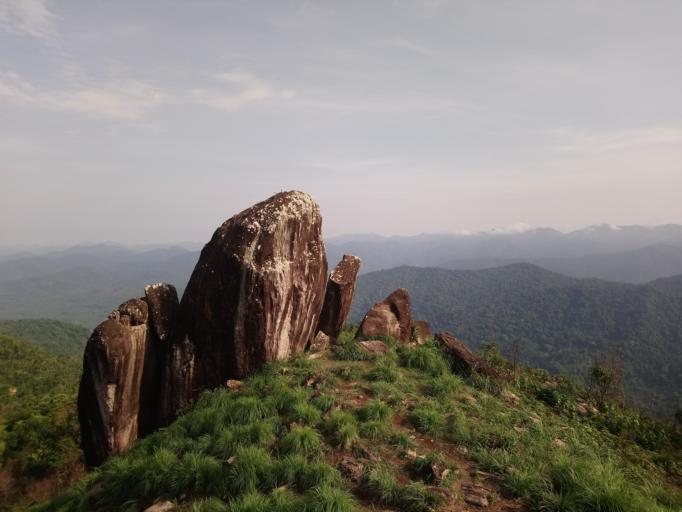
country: IN
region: Kerala
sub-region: Kannur
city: Taliparamba
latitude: 12.2757
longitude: 75.4849
